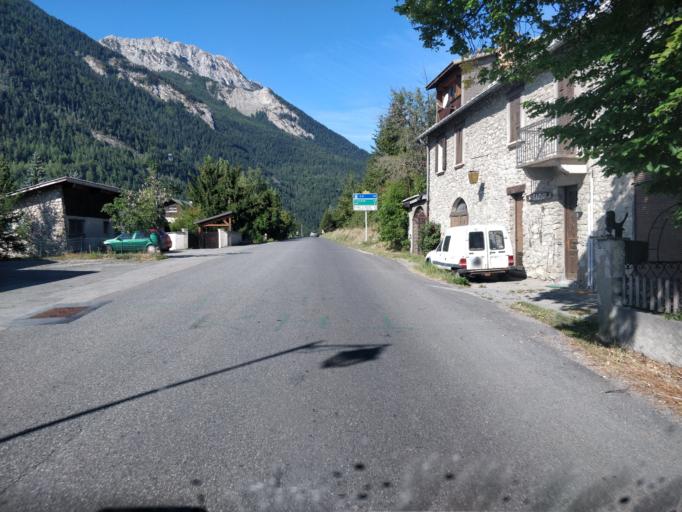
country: FR
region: Provence-Alpes-Cote d'Azur
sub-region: Departement des Alpes-de-Haute-Provence
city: Barcelonnette
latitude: 44.3931
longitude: 6.5693
